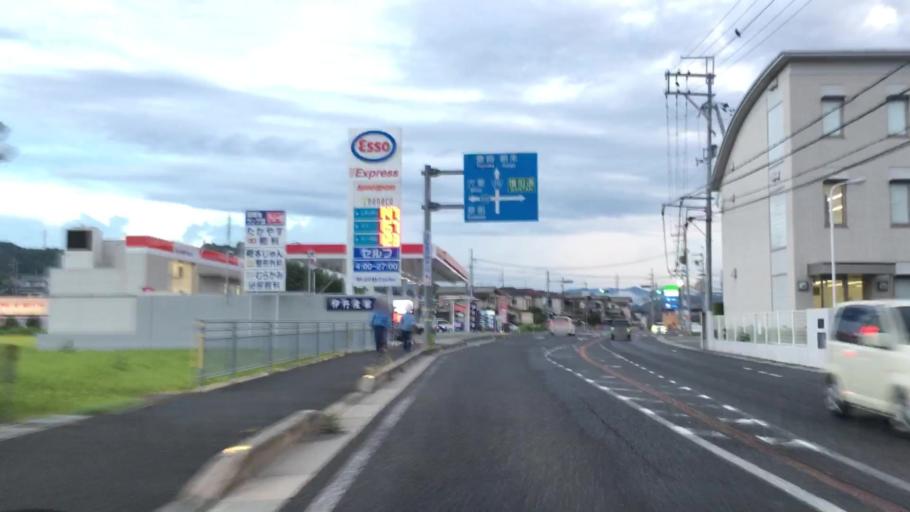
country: JP
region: Hyogo
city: Himeji
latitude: 34.9237
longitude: 134.7440
